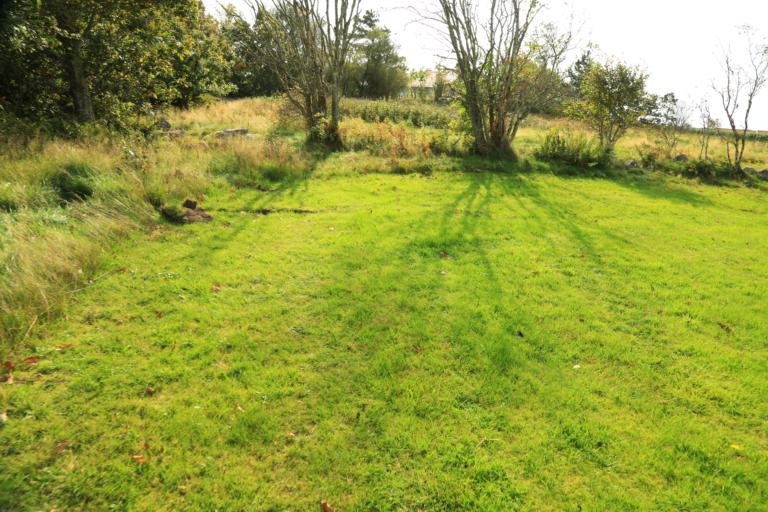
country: SE
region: Halland
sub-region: Varbergs Kommun
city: Varberg
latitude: 57.1181
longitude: 12.2183
